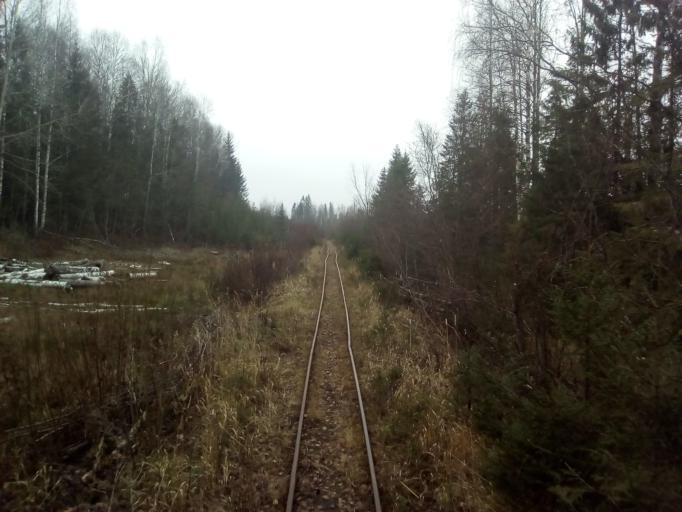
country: RU
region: Vologda
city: Kharovsk
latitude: 59.8032
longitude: 40.4499
